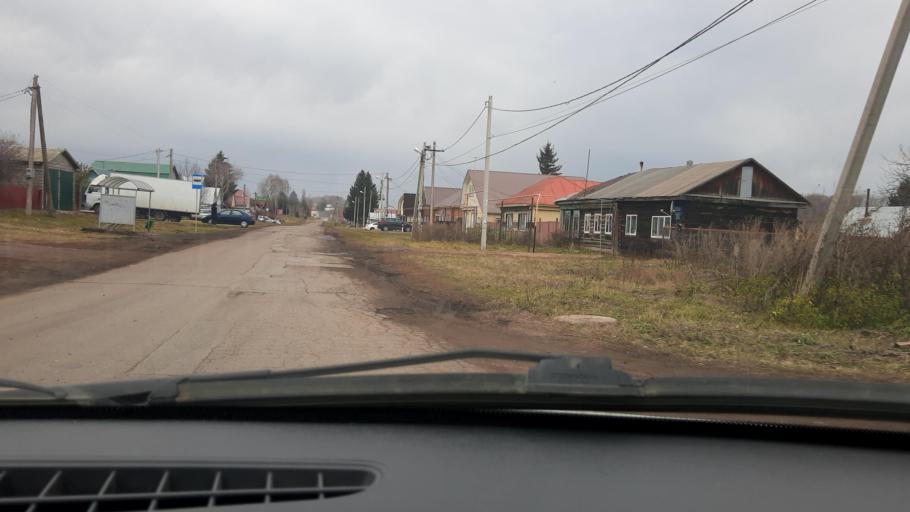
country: RU
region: Bashkortostan
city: Avdon
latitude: 54.7051
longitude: 55.8032
